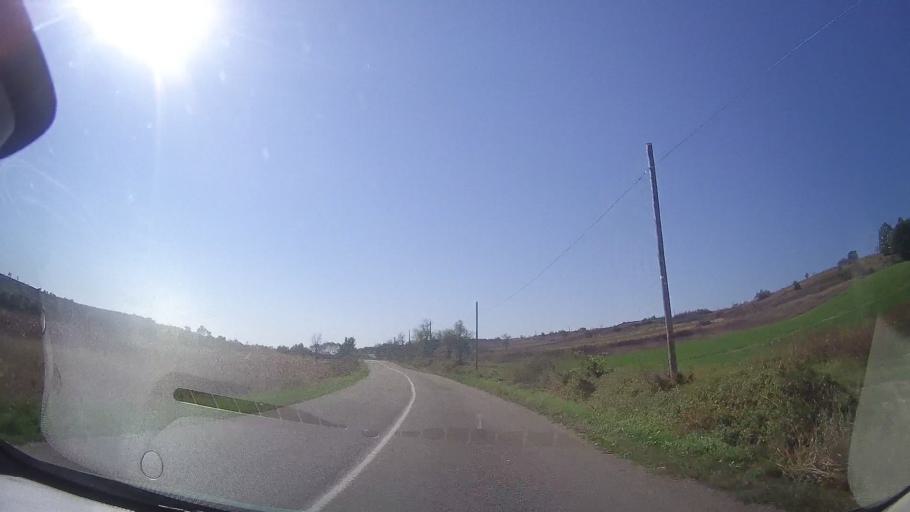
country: RO
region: Timis
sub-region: Comuna Ohaba Lunga
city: Ohaba Lunga
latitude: 45.8994
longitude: 21.9751
